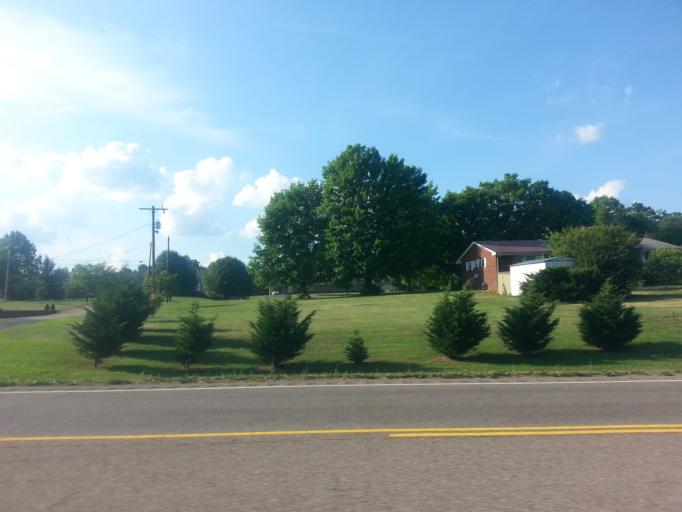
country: US
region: Tennessee
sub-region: Knox County
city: Knoxville
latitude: 35.9011
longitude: -83.8529
